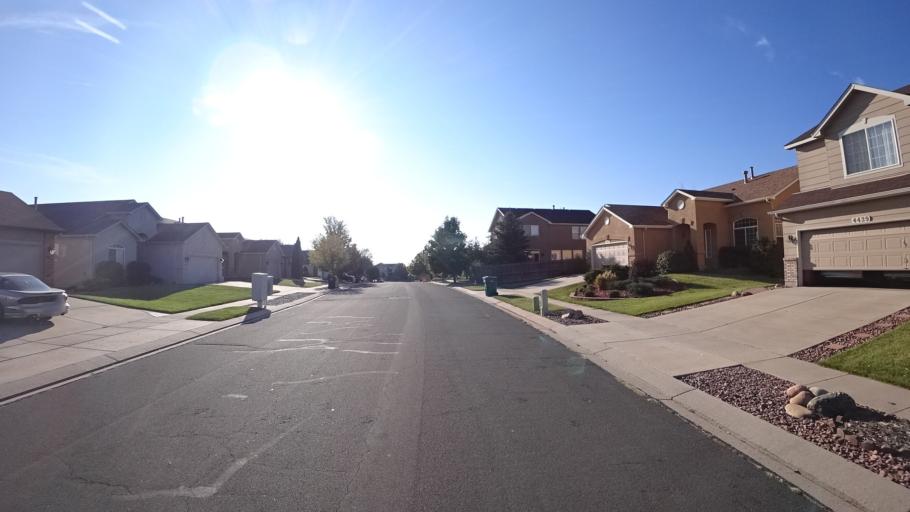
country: US
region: Colorado
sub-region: El Paso County
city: Cimarron Hills
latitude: 38.8920
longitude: -104.6996
